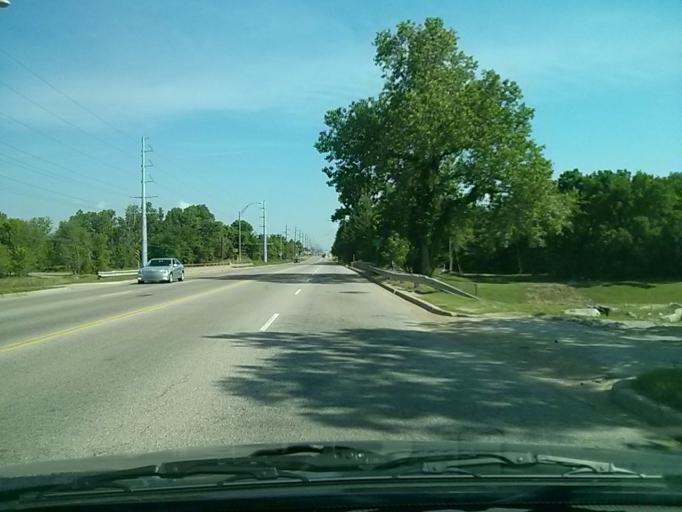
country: US
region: Oklahoma
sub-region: Tulsa County
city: Turley
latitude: 36.2126
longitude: -95.9755
